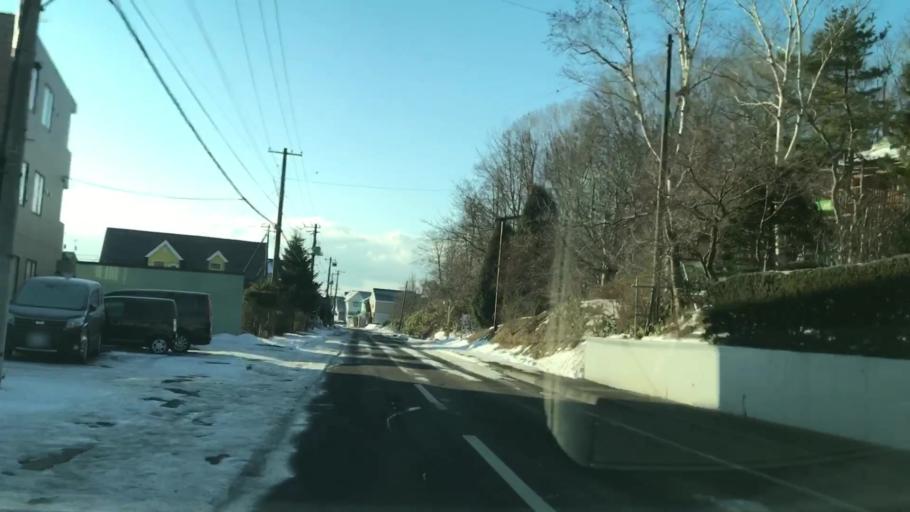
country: JP
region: Hokkaido
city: Muroran
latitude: 42.3887
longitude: 141.0654
